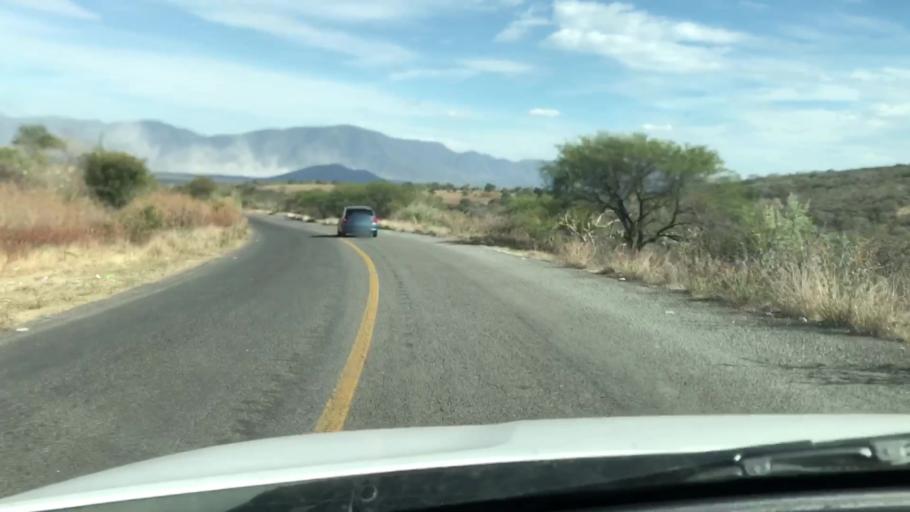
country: MX
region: Jalisco
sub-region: Zacoalco de Torres
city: Barranca de Otates (Barranca de Otatan)
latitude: 20.2586
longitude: -103.6556
